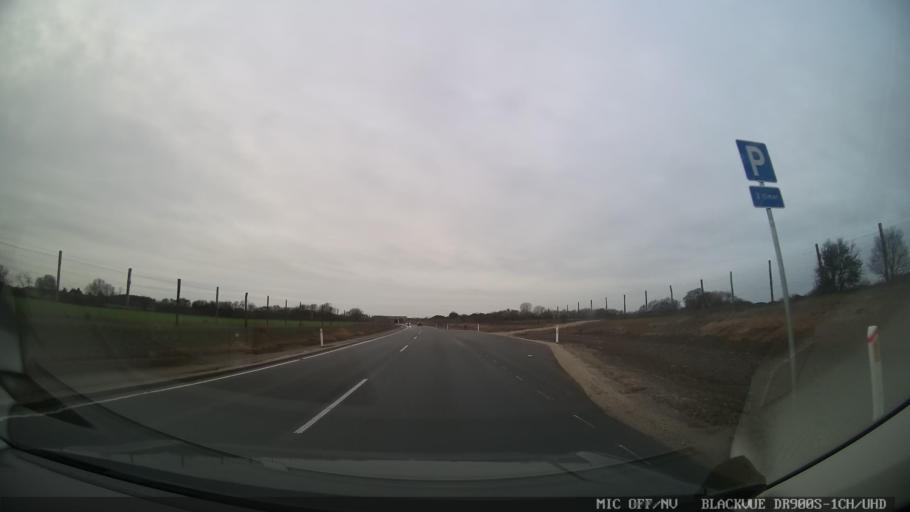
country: DK
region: Central Jutland
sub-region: Arhus Kommune
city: Malling
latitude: 56.0543
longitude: 10.1834
